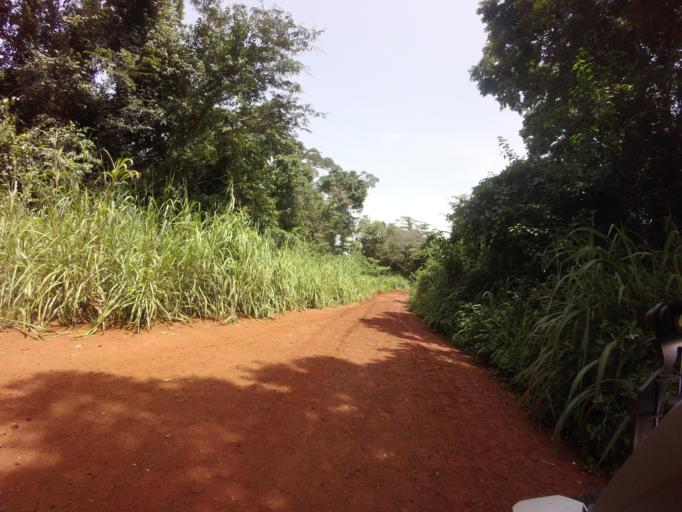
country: GN
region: Nzerekore
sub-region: Lola
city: Lola
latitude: 7.7283
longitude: -8.3913
